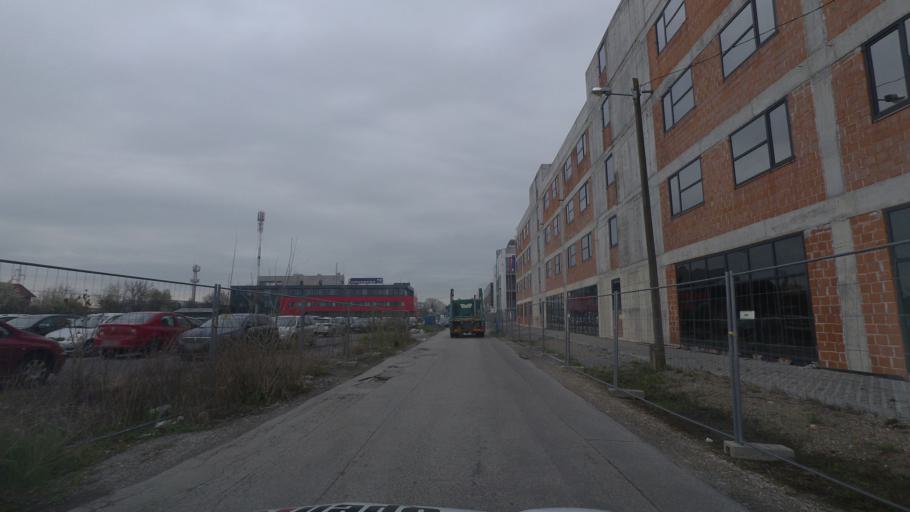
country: HR
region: Grad Zagreb
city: Odra
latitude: 45.7486
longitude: 15.9970
